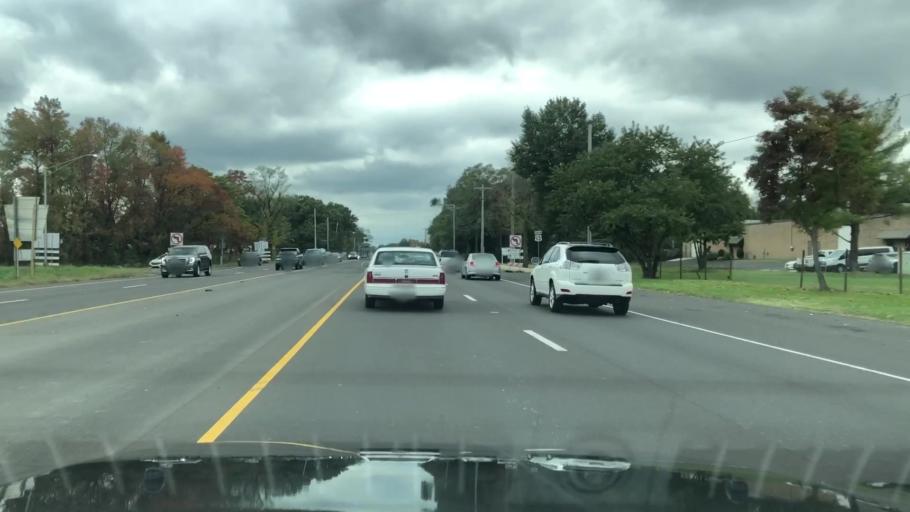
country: US
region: Pennsylvania
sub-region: Bucks County
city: Bristol
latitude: 40.1166
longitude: -74.8471
